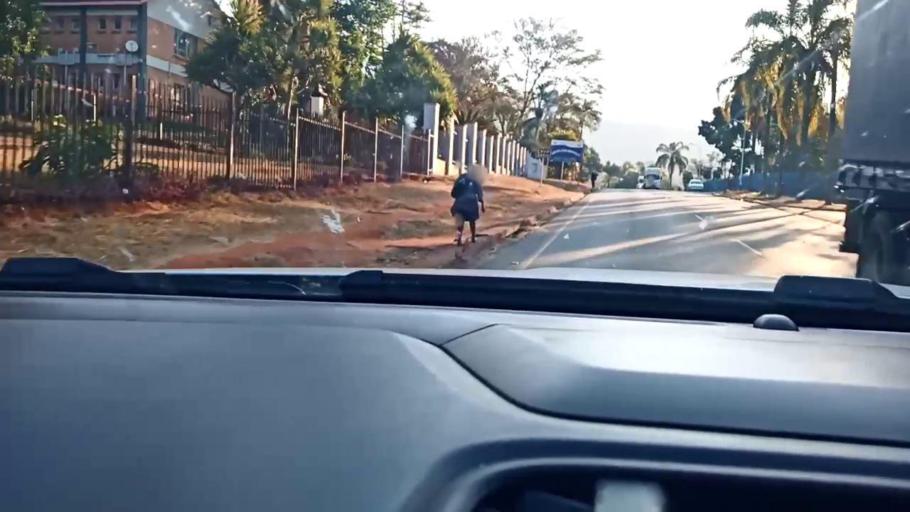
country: ZA
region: Limpopo
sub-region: Mopani District Municipality
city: Duiwelskloof
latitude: -23.6952
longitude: 30.1458
